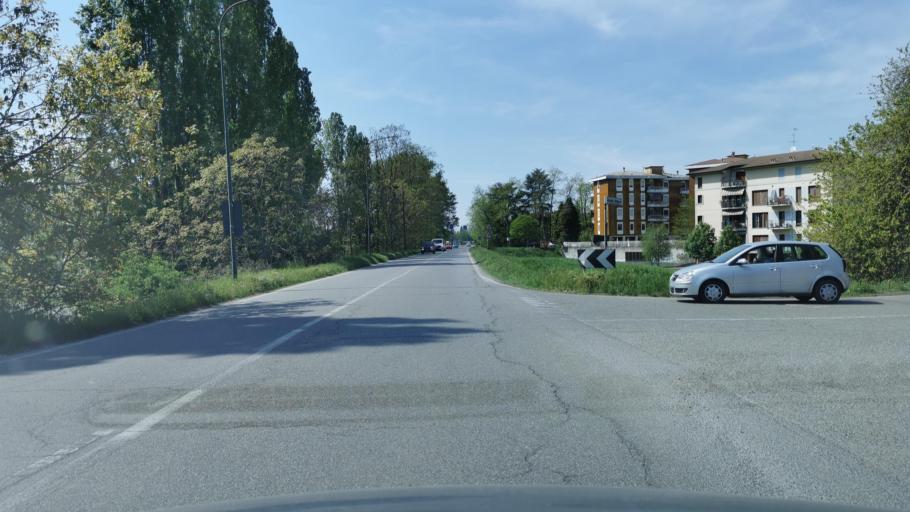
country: IT
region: Lombardy
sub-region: Provincia di Cremona
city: Cremona
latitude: 45.1274
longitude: 10.0088
